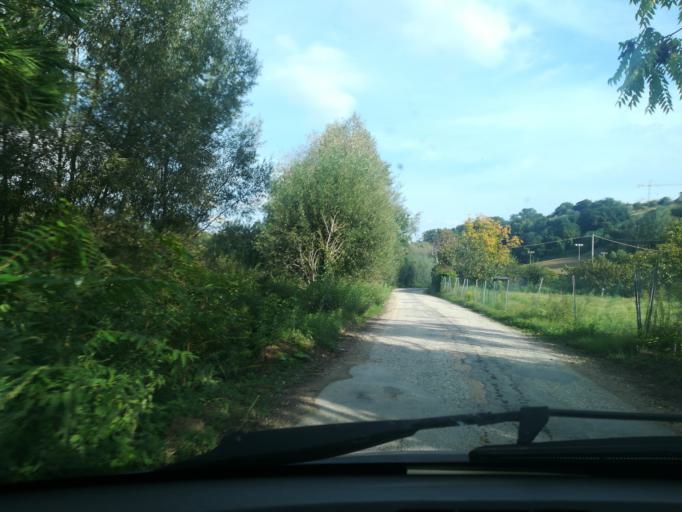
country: IT
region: The Marches
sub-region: Provincia di Macerata
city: Macerata
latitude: 43.3164
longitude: 13.4597
